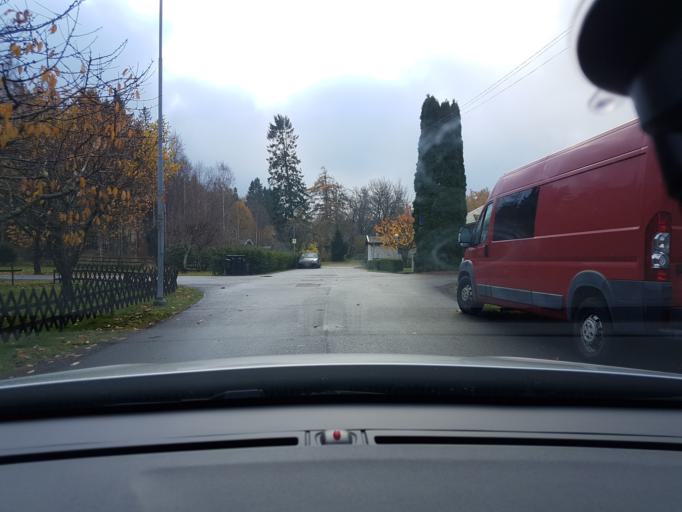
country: SE
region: Vaestra Goetaland
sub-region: Ale Kommun
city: Surte
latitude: 57.8206
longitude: 12.0254
